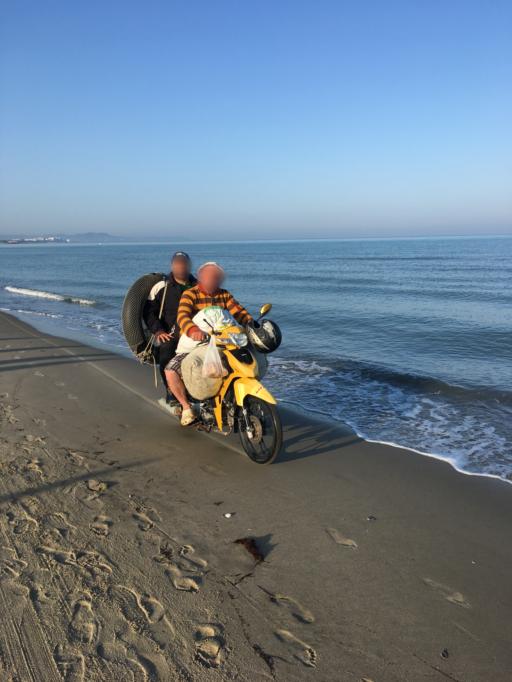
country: AL
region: Tirane
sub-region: Rrethi i Kavajes
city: Golem
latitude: 41.2511
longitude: 19.5190
